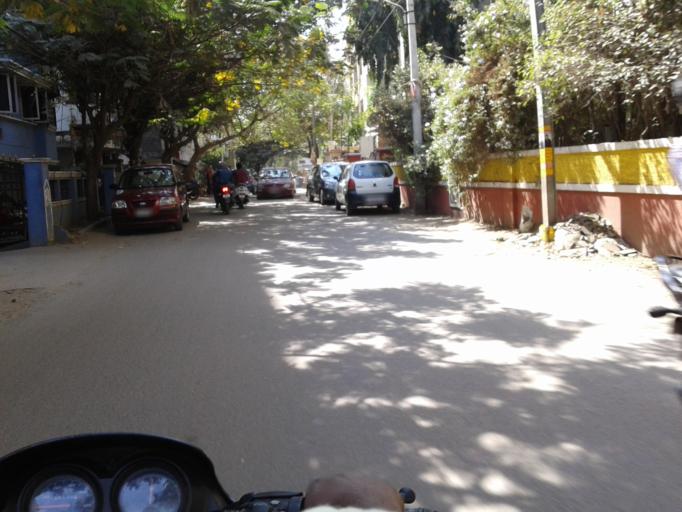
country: IN
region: Telangana
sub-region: Rangareddi
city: Kukatpalli
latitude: 17.4350
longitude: 78.4363
